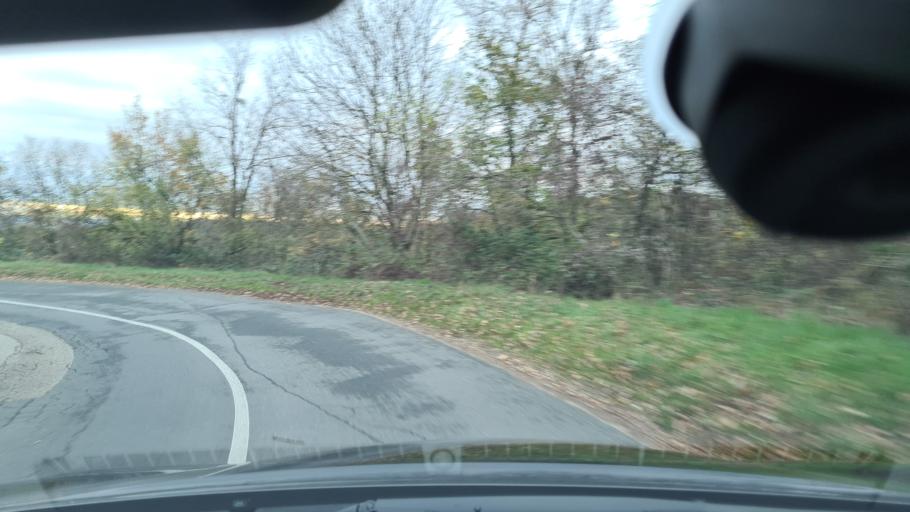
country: FR
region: Rhone-Alpes
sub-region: Departement du Rhone
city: Limonest
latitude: 45.8495
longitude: 4.7821
